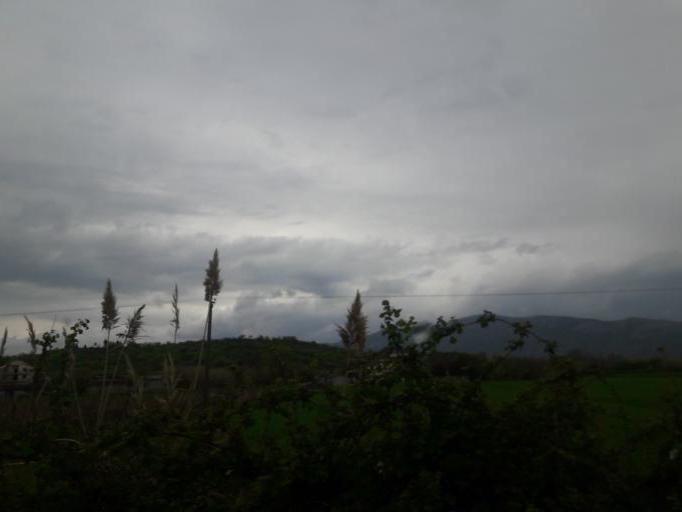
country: AL
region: Shkoder
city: Vukatane
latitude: 42.0066
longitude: 19.5354
